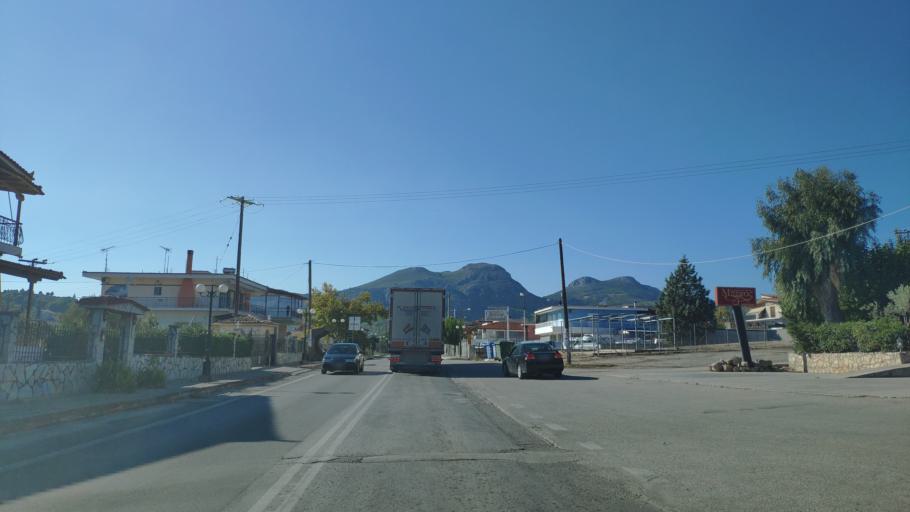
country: GR
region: Peloponnese
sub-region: Nomos Korinthias
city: Arkhaia Korinthos
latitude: 37.8821
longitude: 22.8913
